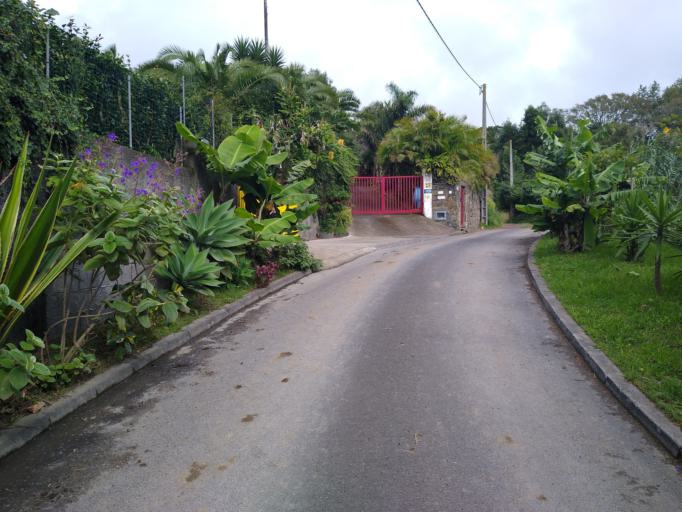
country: PT
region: Azores
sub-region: Ponta Delgada
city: Arrifes
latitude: 37.8396
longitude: -25.8255
